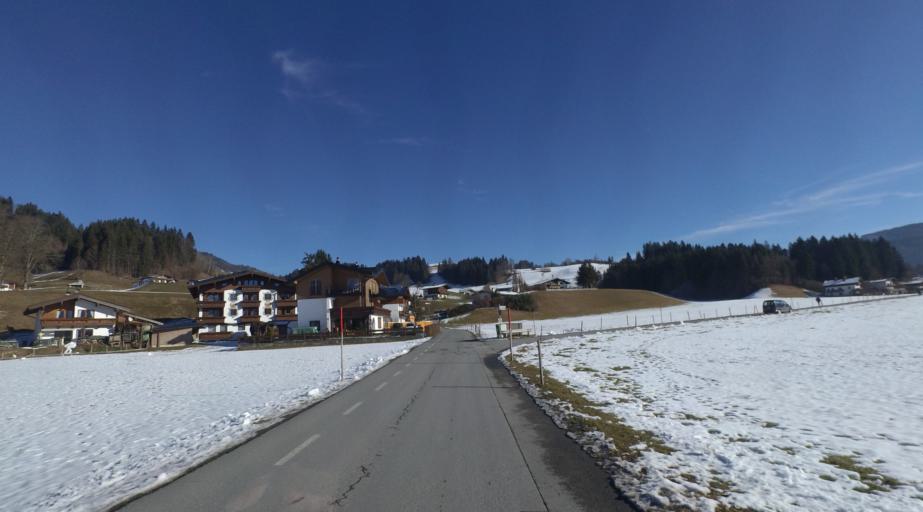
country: AT
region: Tyrol
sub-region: Politischer Bezirk Kitzbuhel
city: Kossen
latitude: 47.6707
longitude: 12.4104
